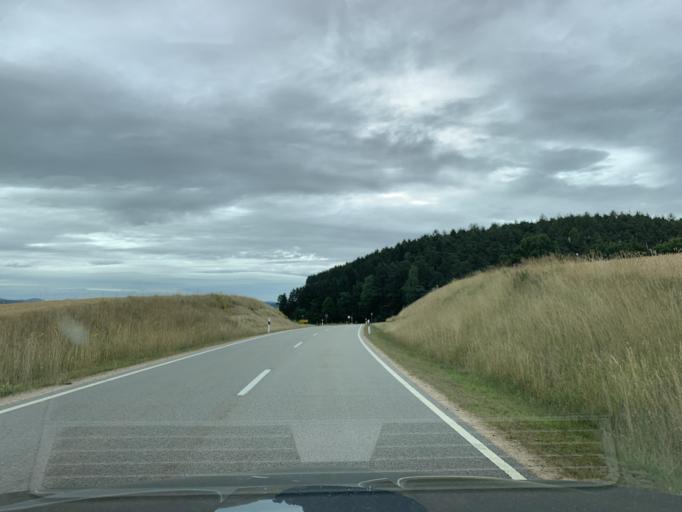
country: DE
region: Bavaria
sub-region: Upper Palatinate
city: Pettendorf
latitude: 49.3612
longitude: 12.3459
